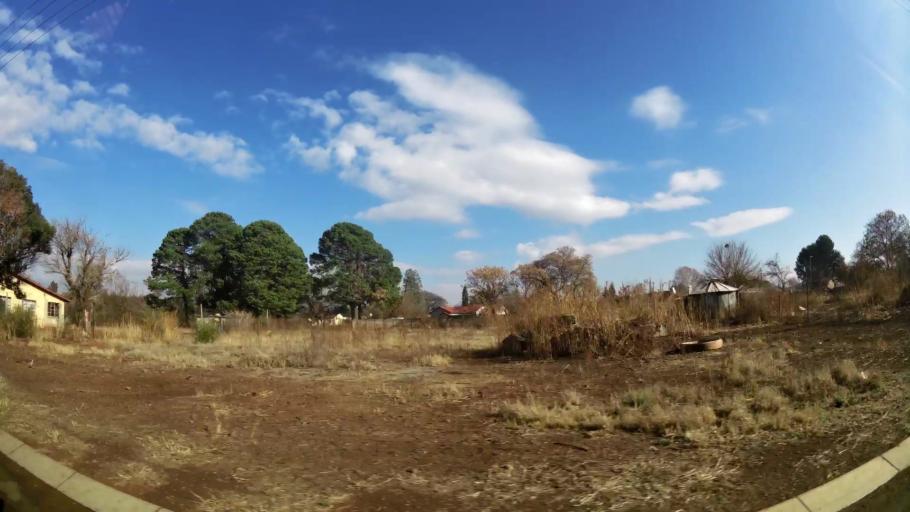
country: ZA
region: Gauteng
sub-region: Sedibeng District Municipality
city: Meyerton
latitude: -26.5053
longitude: 28.0695
